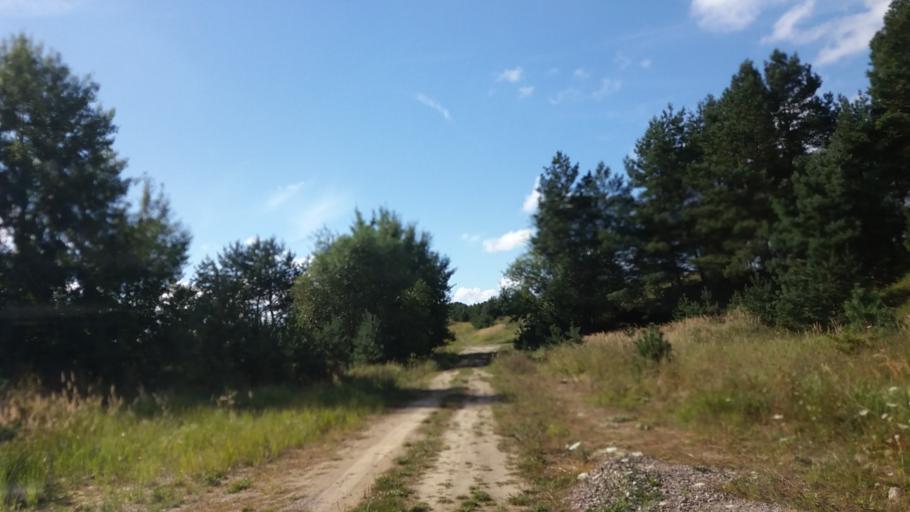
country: PL
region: West Pomeranian Voivodeship
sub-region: Powiat choszczenski
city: Krzecin
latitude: 53.1286
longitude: 15.4998
